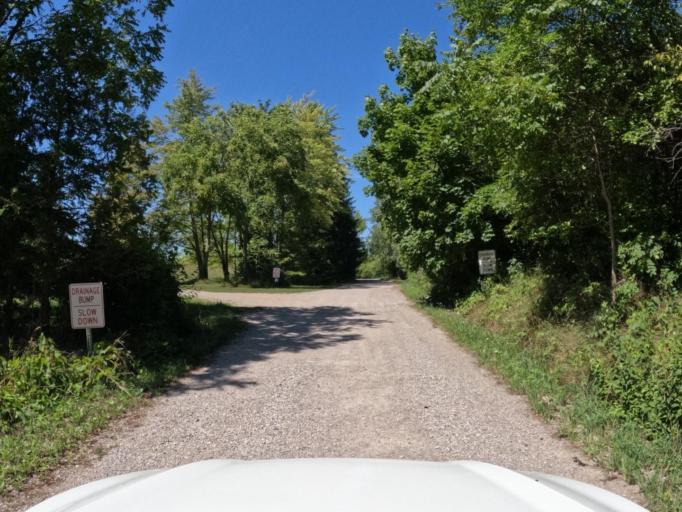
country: CA
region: Ontario
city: Cambridge
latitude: 43.4110
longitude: -80.2550
